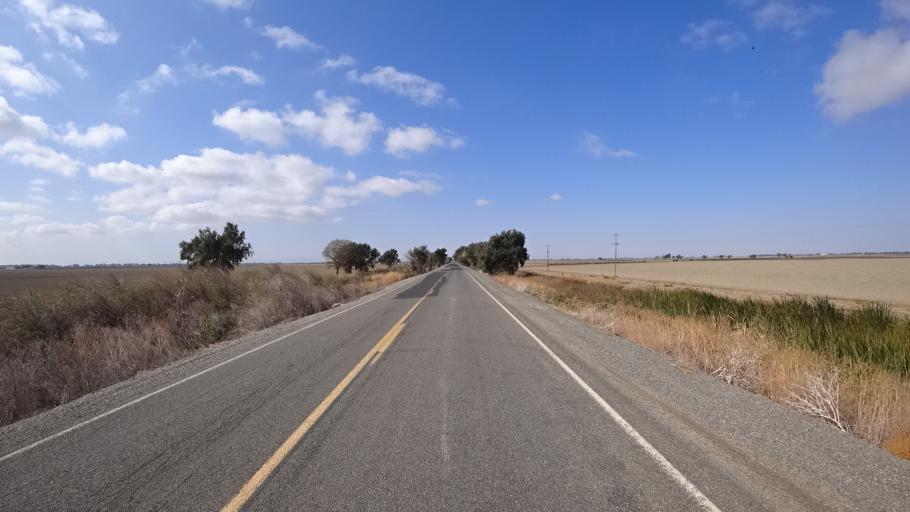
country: US
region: California
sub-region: Yolo County
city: Woodland
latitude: 38.7486
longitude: -121.6969
